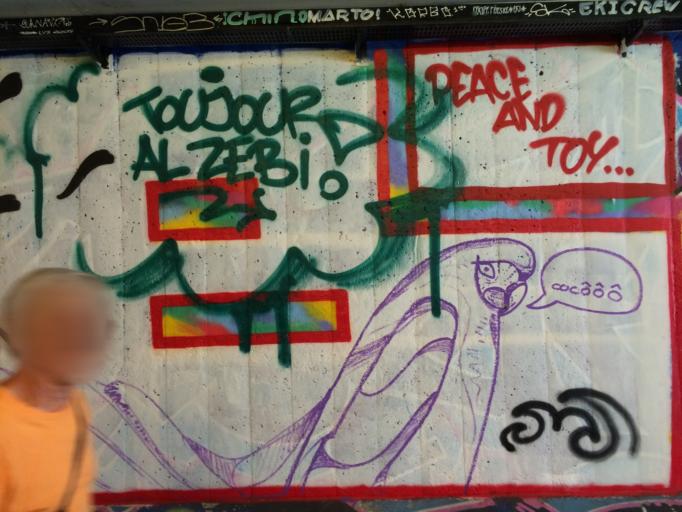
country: CH
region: Geneva
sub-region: Geneva
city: Geneve
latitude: 46.2035
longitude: 6.1322
